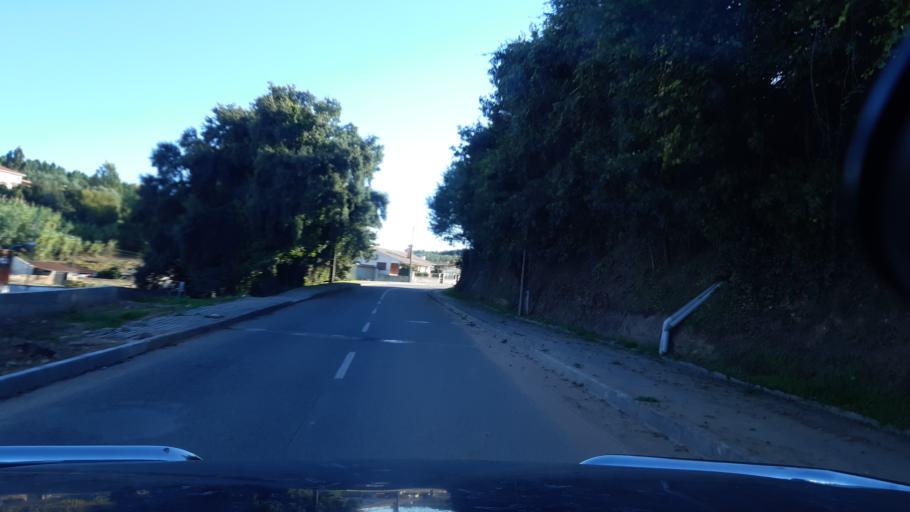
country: PT
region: Aveiro
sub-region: Agueda
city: Agueda
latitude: 40.5549
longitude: -8.4419
